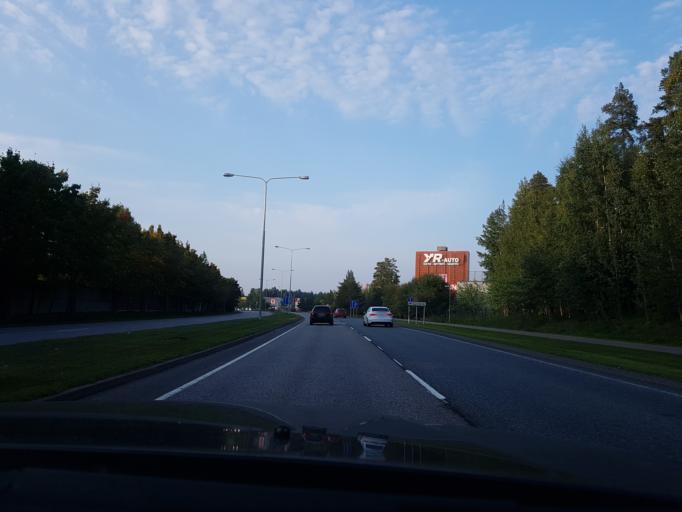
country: FI
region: Uusimaa
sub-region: Helsinki
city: Tuusula
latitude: 60.3813
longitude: 25.0250
